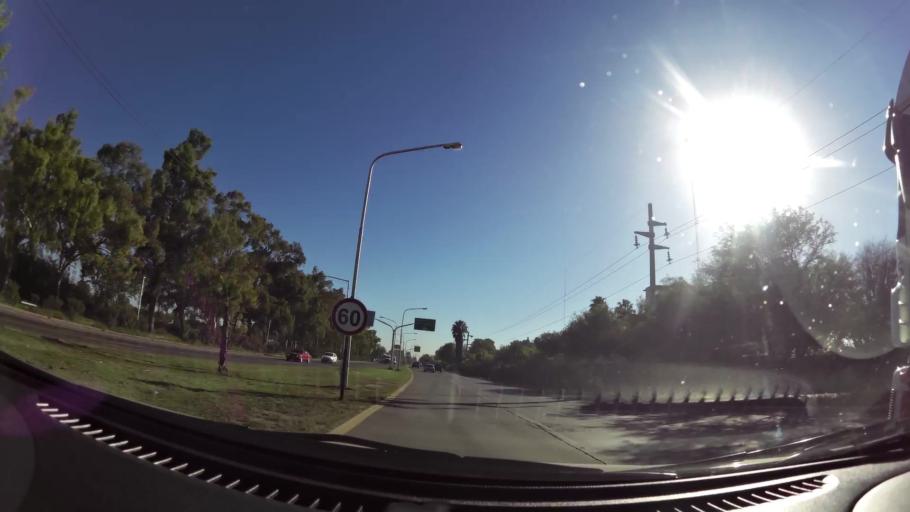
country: AR
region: Mendoza
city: Las Heras
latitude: -32.8696
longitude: -68.8144
